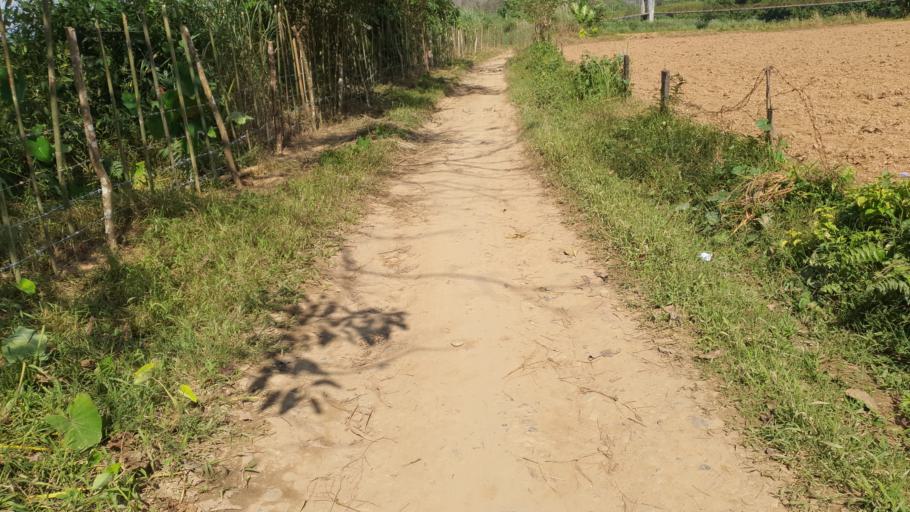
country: LA
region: Bolikhamxai
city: Bolikhan
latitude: 18.9077
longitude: 103.7428
